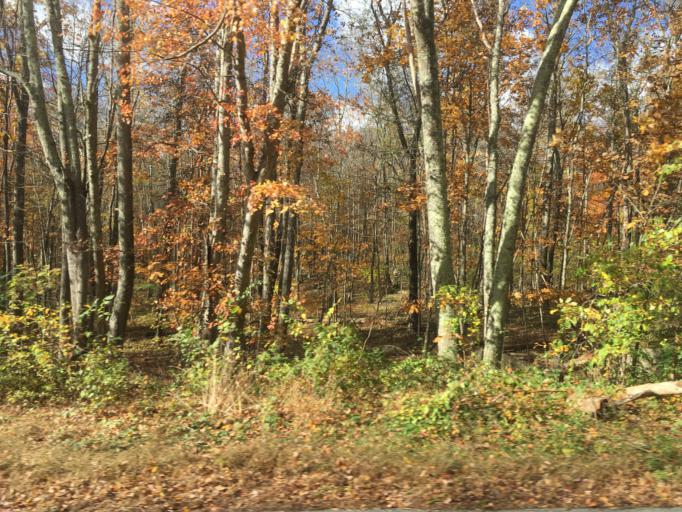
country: US
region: Rhode Island
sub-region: Providence County
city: North Scituate
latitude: 41.8035
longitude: -71.6583
